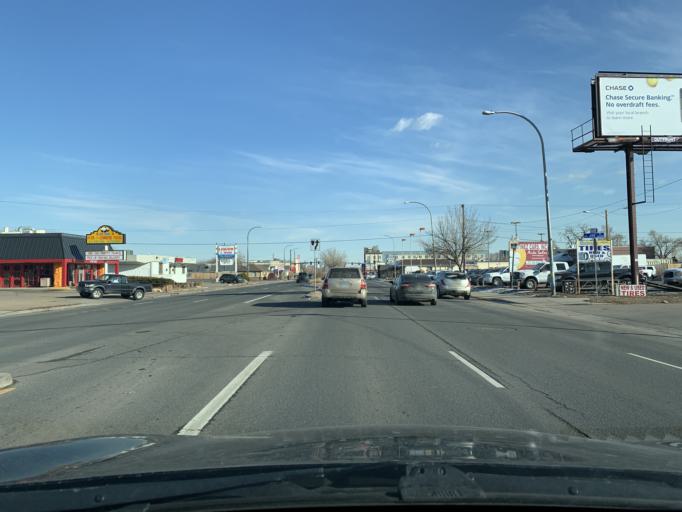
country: US
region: Colorado
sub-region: Jefferson County
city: Edgewater
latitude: 39.7403
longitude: -105.0652
